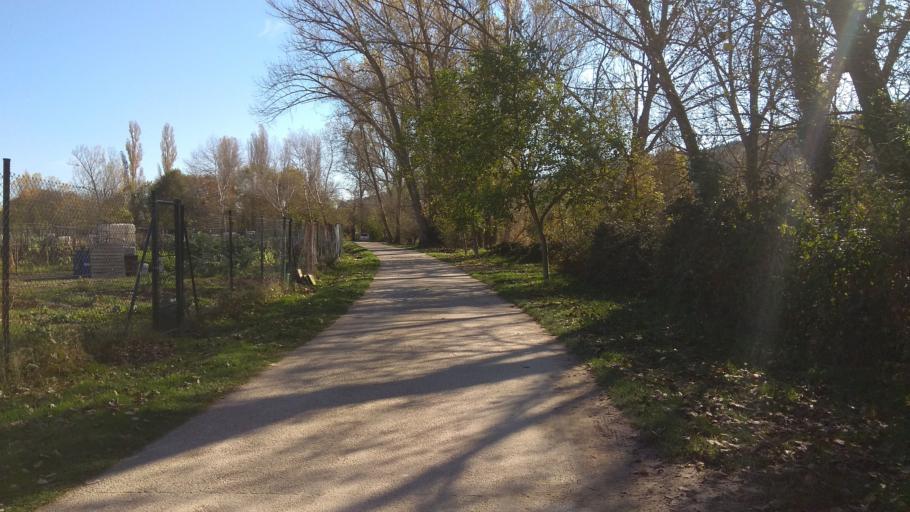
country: ES
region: Navarre
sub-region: Provincia de Navarra
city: Cizur Mayor
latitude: 42.7982
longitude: -1.6938
